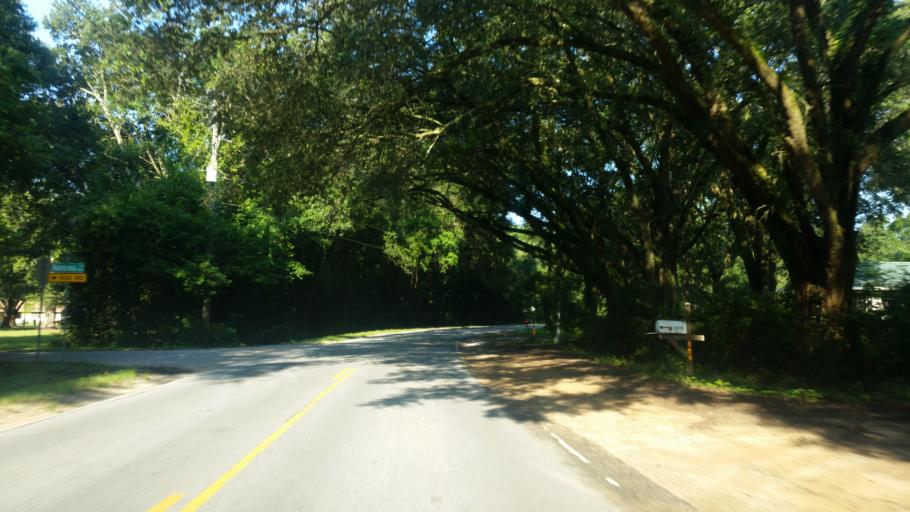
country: US
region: Florida
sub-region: Escambia County
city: Bellview
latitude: 30.4480
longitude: -87.3223
